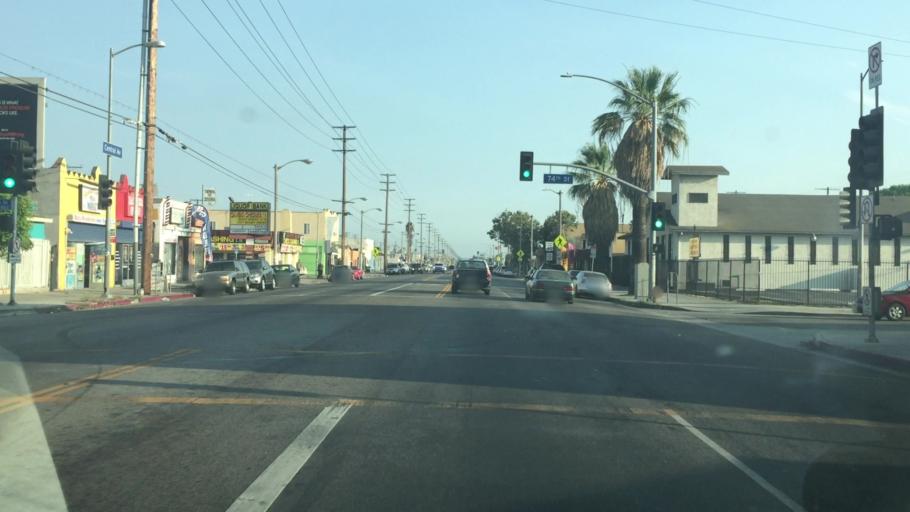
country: US
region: California
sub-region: Los Angeles County
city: Florence-Graham
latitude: 33.9733
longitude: -118.2564
